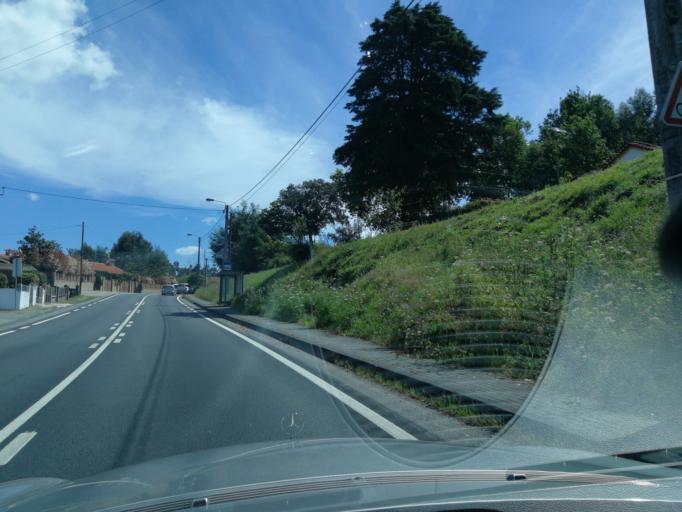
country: PT
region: Braga
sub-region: Vila Nova de Famalicao
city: Calendario
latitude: 41.4209
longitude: -8.5361
